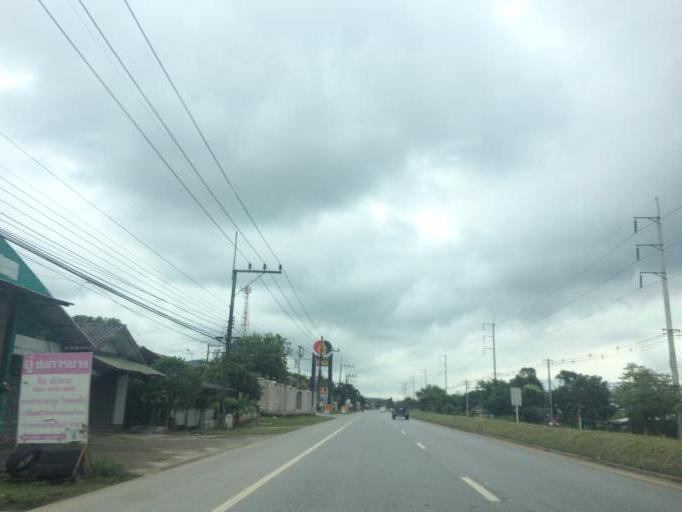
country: TH
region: Chiang Rai
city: Mae Chan
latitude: 20.0809
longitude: 99.8749
